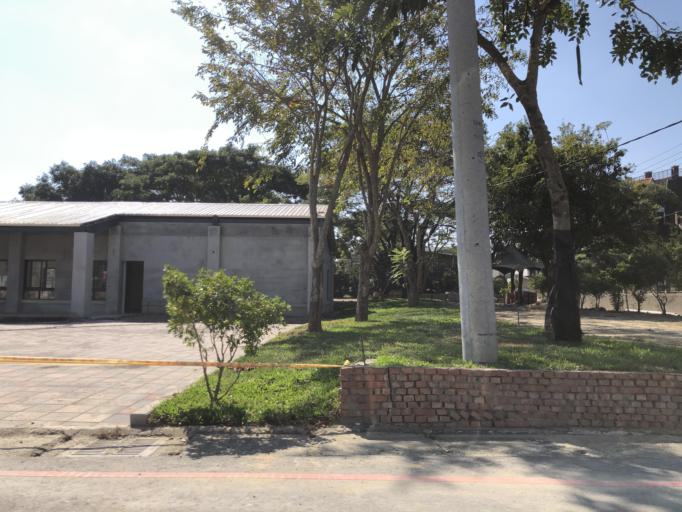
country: TW
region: Taiwan
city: Yujing
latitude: 23.0635
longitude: 120.3884
